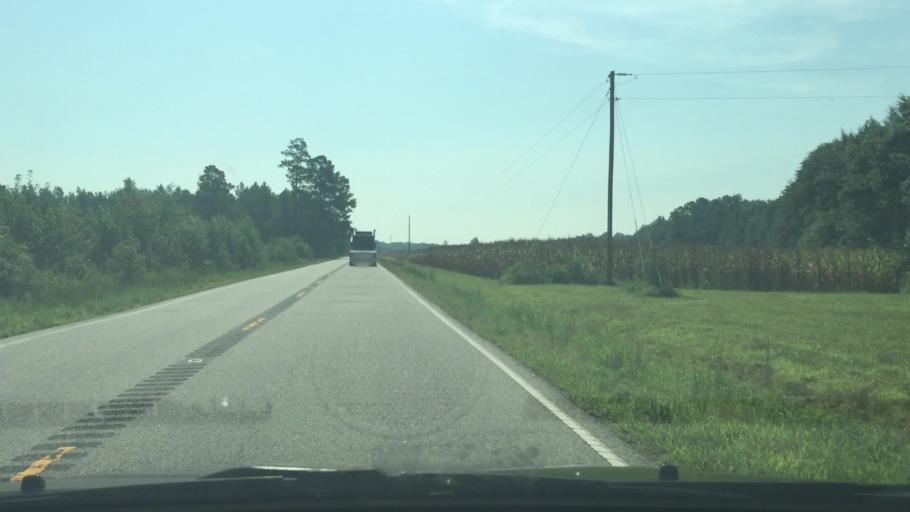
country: US
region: Virginia
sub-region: Sussex County
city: Sussex
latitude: 36.9820
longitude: -77.2389
